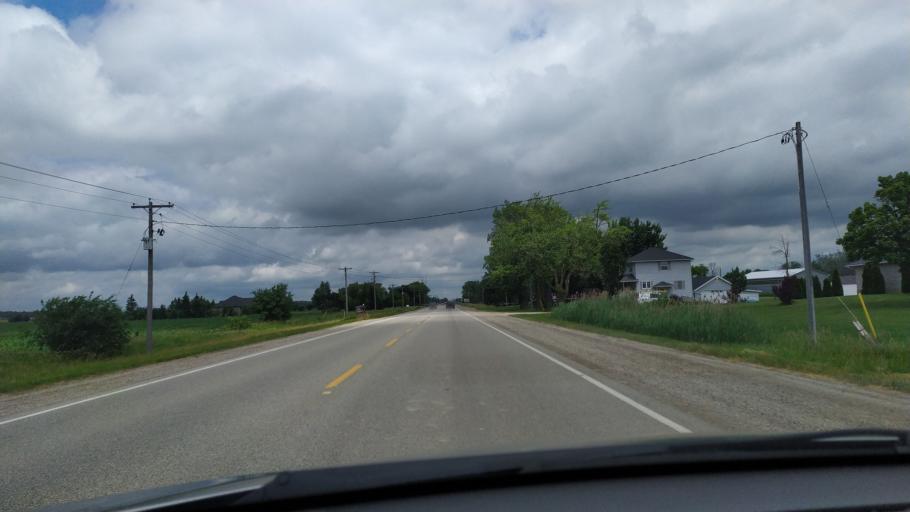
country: CA
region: Ontario
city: Stratford
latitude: 43.3965
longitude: -80.9619
